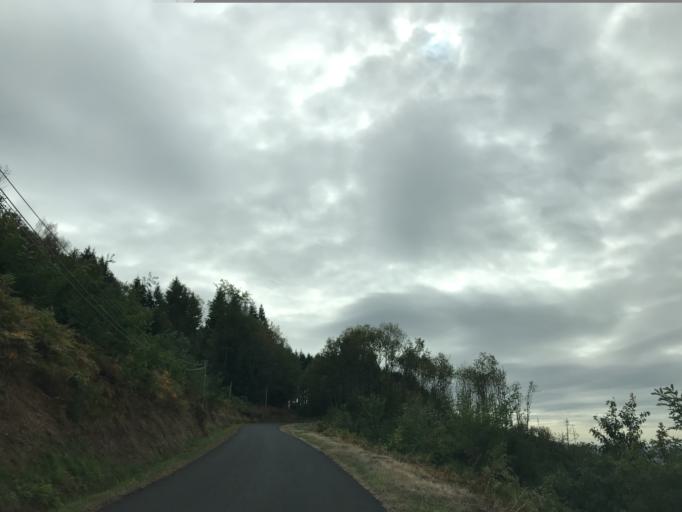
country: FR
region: Auvergne
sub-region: Departement du Puy-de-Dome
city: Escoutoux
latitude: 45.8322
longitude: 3.5790
